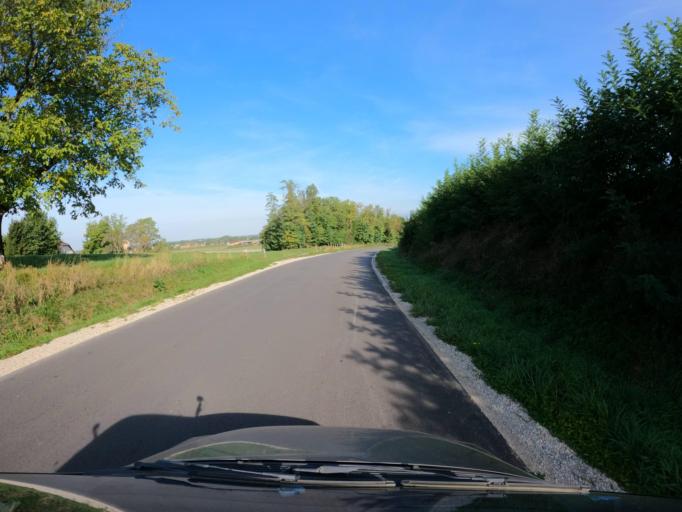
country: FR
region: Franche-Comte
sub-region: Departement du Jura
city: Bletterans
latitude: 46.7325
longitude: 5.5035
